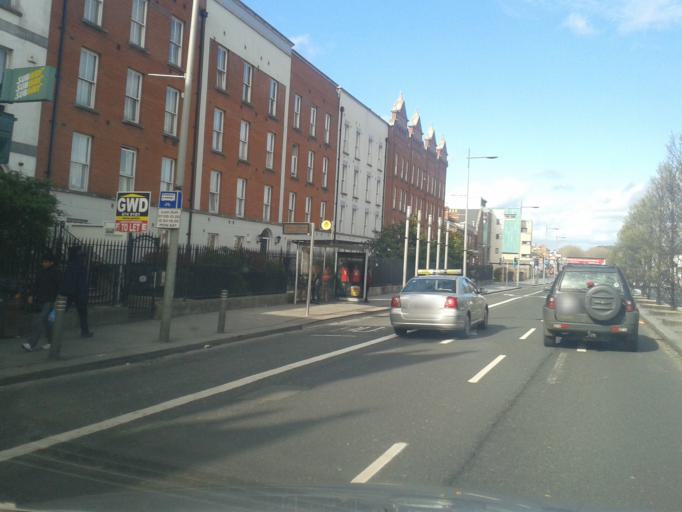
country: IE
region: Leinster
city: Drumcondra
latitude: 53.3600
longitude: -6.2611
